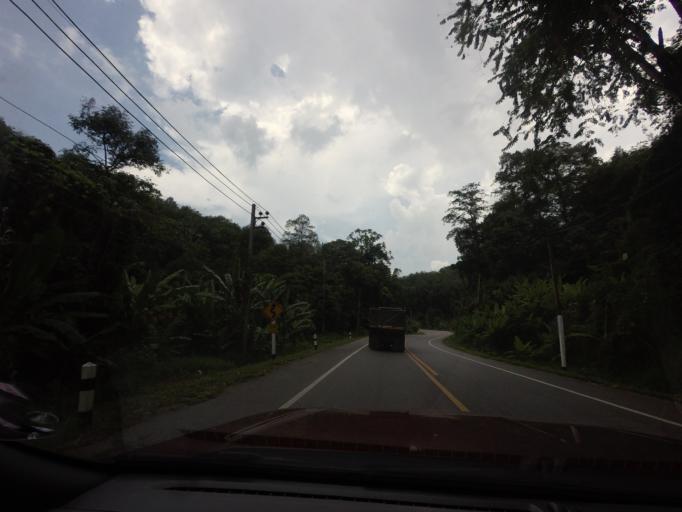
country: TH
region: Yala
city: Than To
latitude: 6.0822
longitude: 101.1849
